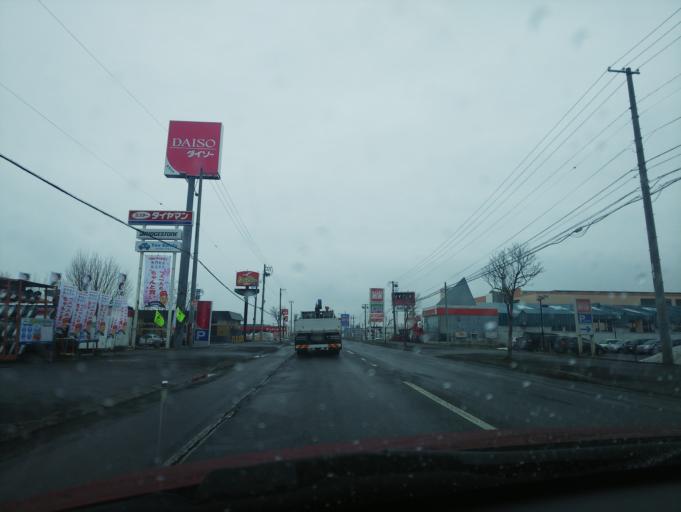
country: JP
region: Hokkaido
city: Nayoro
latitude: 44.1644
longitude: 142.3959
